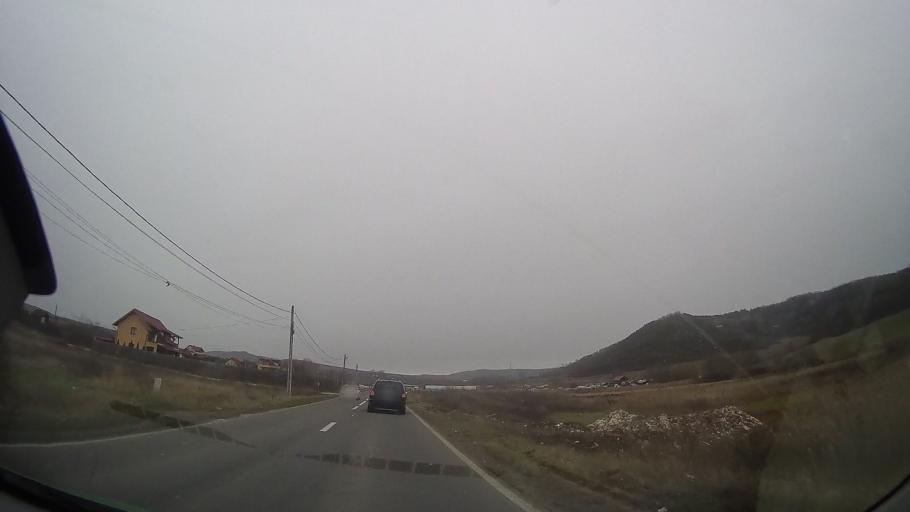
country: RO
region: Mures
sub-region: Comuna Ceausu de Campie
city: Ceausu de Campie
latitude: 46.6299
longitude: 24.5197
